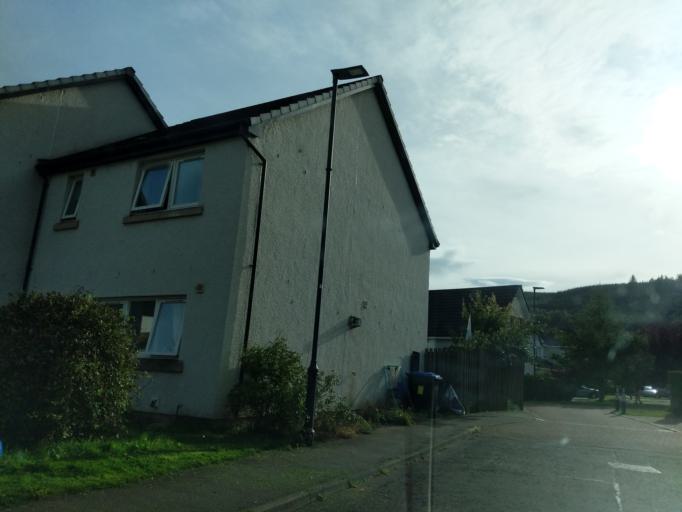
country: GB
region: Scotland
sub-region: The Scottish Borders
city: Innerleithen
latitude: 55.6357
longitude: -3.1037
